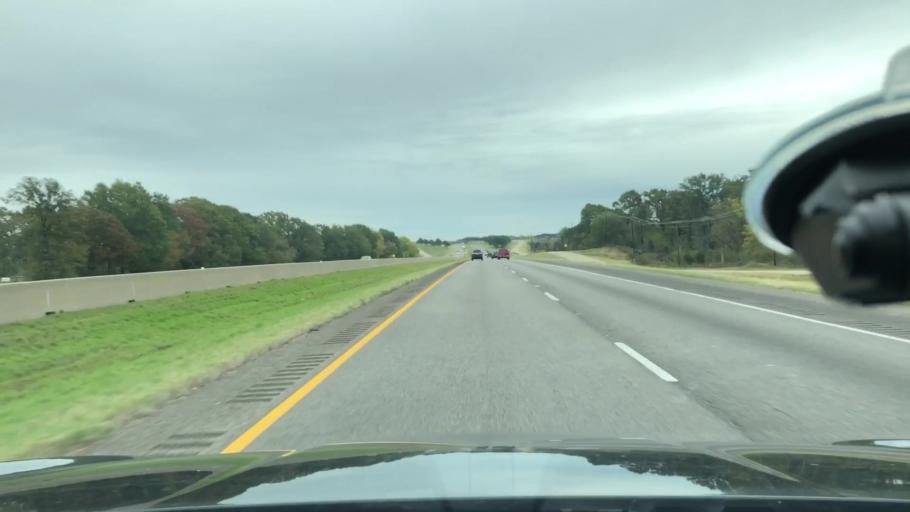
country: US
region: Texas
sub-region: Hopkins County
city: Sulphur Springs
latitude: 33.1466
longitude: -95.4716
